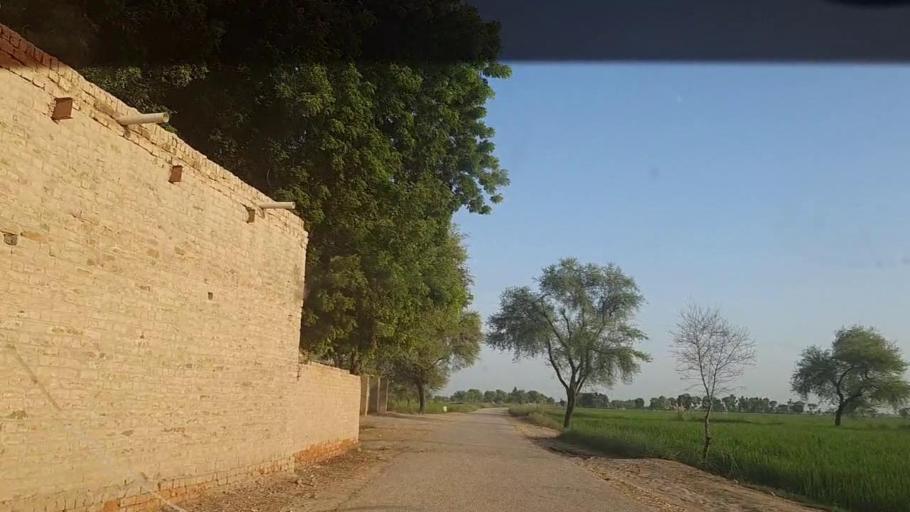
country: PK
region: Sindh
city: Thul
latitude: 28.1287
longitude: 68.8925
